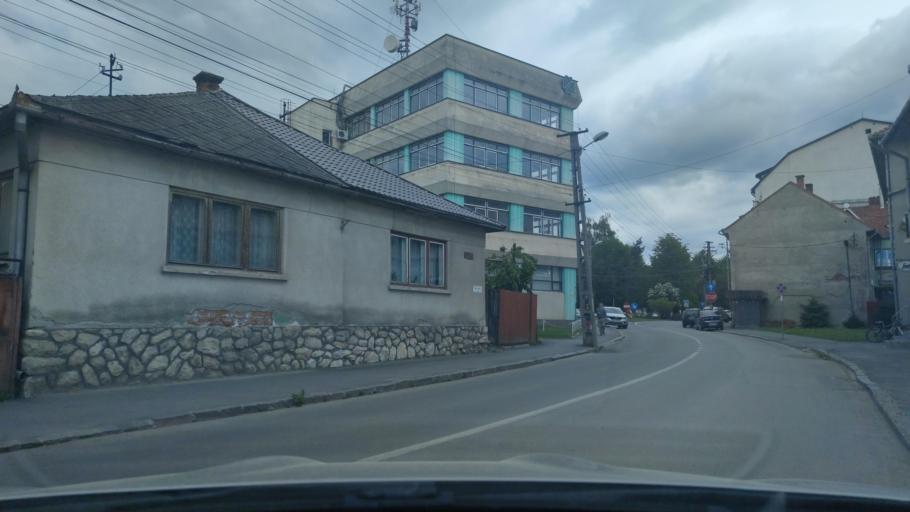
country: RO
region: Harghita
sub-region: Municipiul Gheorgheni
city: Gheorgheni
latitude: 46.7201
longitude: 25.5989
